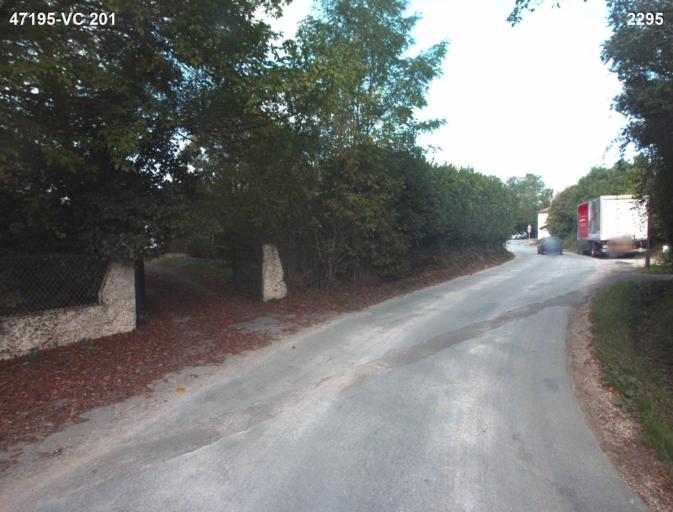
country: FR
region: Aquitaine
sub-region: Departement du Lot-et-Garonne
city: Barbaste
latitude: 44.1342
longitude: 0.2939
